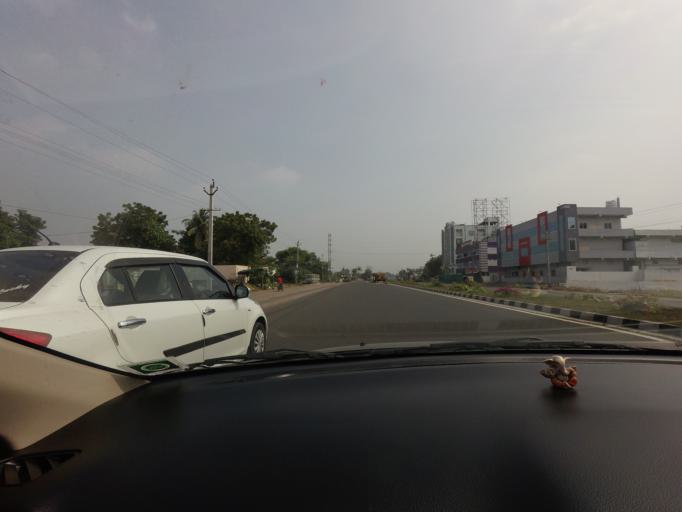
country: IN
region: Andhra Pradesh
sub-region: Krishna
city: Yanamalakuduru
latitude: 16.4708
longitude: 80.7220
